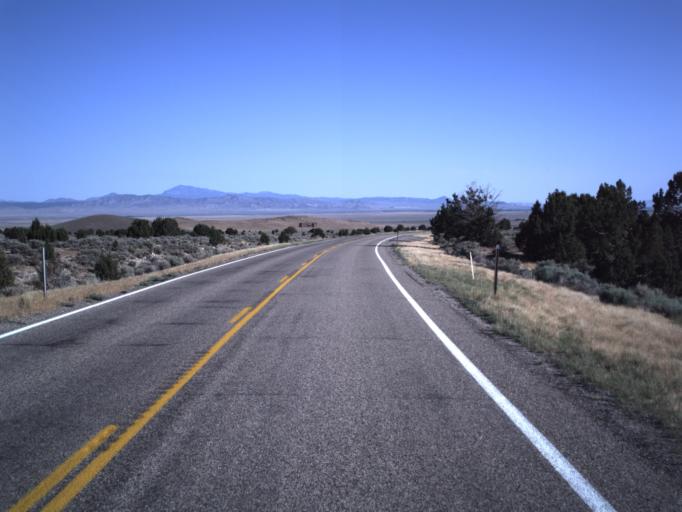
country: US
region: Utah
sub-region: Beaver County
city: Milford
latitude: 38.1293
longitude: -112.9584
